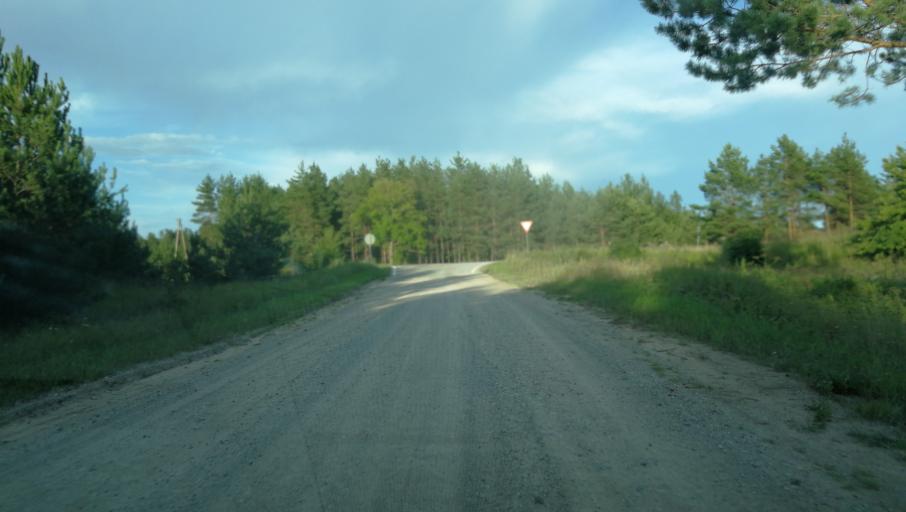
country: LV
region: Krimulda
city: Ragana
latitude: 57.2103
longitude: 24.7799
